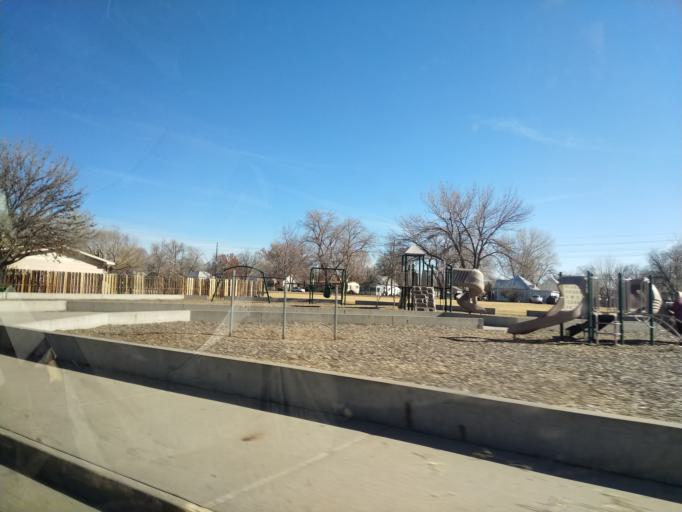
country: US
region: Colorado
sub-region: Mesa County
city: Fruita
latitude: 39.1559
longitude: -108.7299
